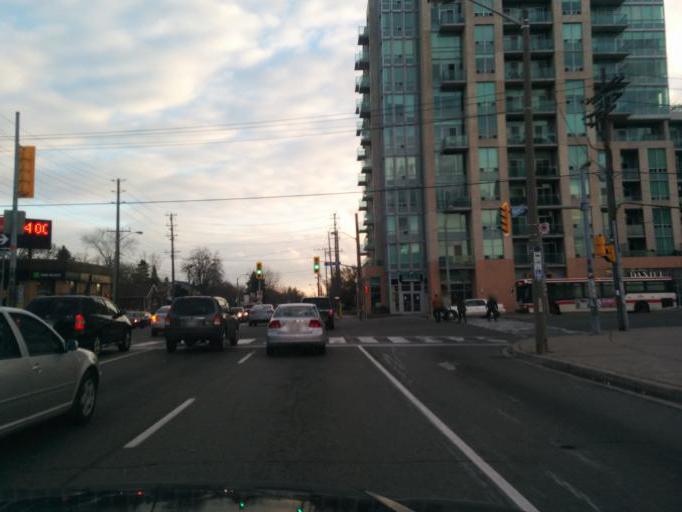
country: CA
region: Ontario
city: Etobicoke
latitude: 43.6450
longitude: -79.5238
